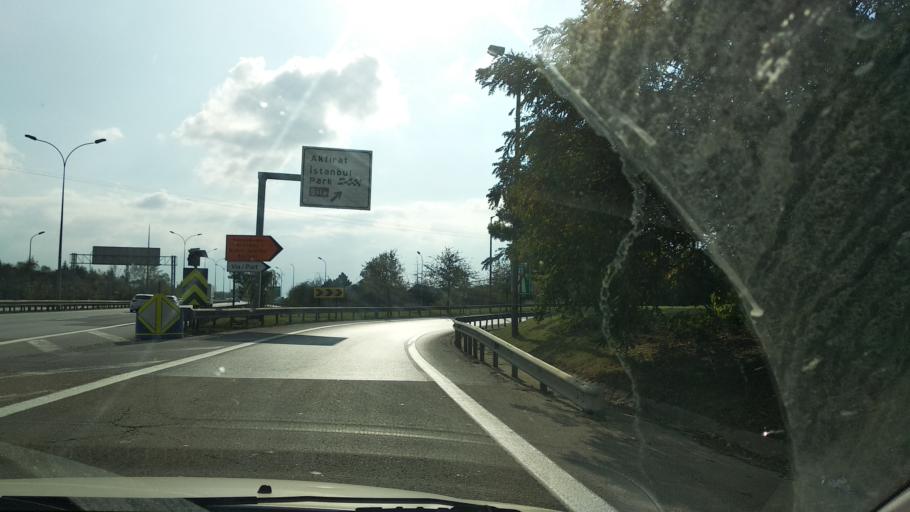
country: TR
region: Istanbul
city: Sultanbeyli
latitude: 40.9298
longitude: 29.3281
